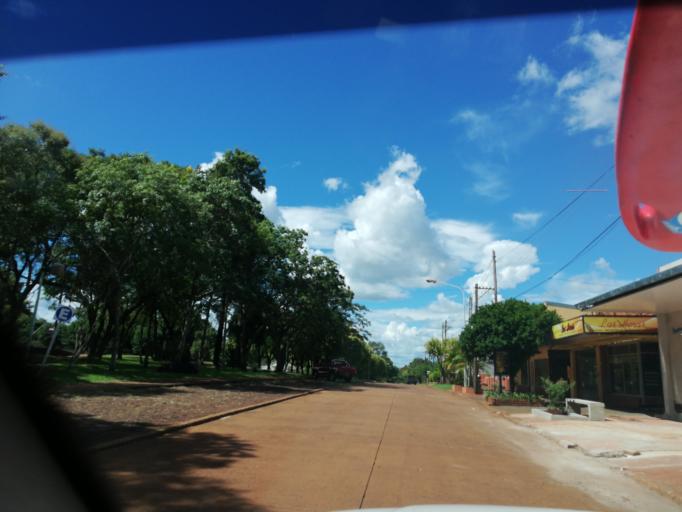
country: AR
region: Misiones
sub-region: Departamento de Apostoles
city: Apostoles
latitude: -27.9139
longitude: -55.7472
